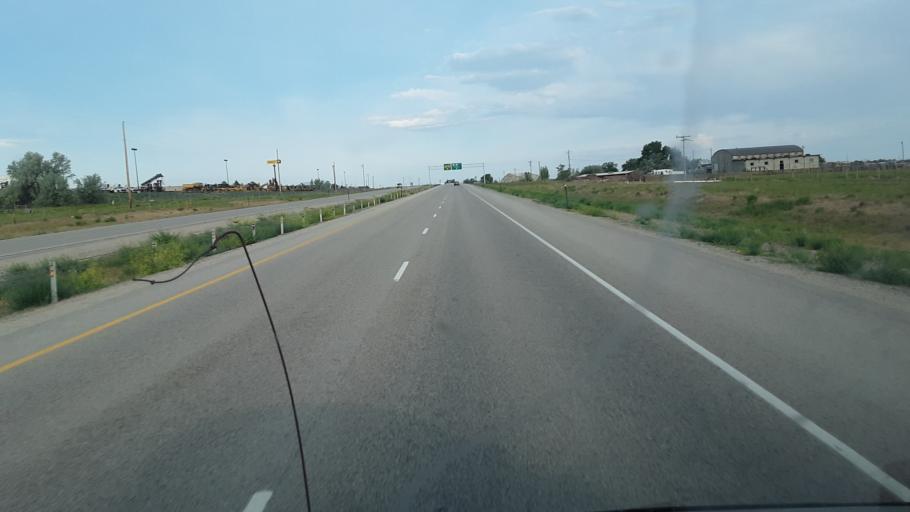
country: US
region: Wyoming
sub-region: Natrona County
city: Mills
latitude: 42.8627
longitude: -106.3884
